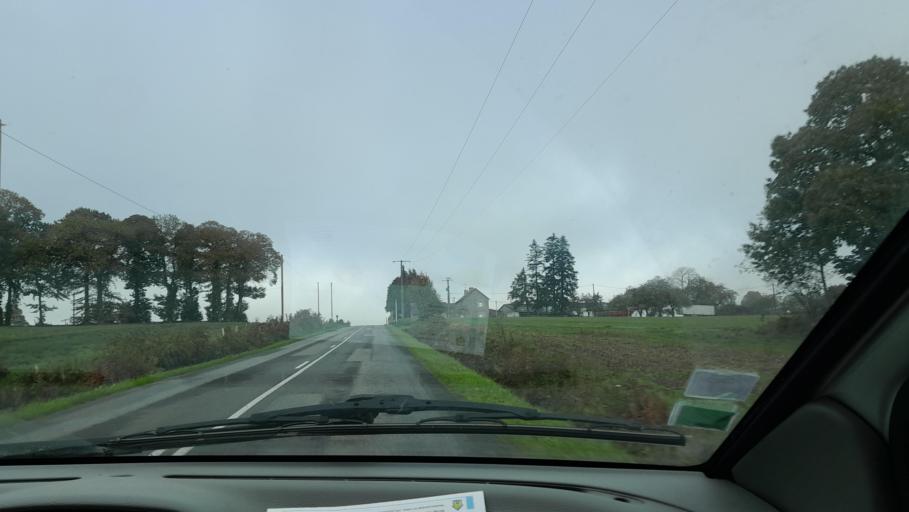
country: FR
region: Brittany
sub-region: Departement d'Ille-et-Vilaine
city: Luitre
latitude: 48.2475
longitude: -1.1204
